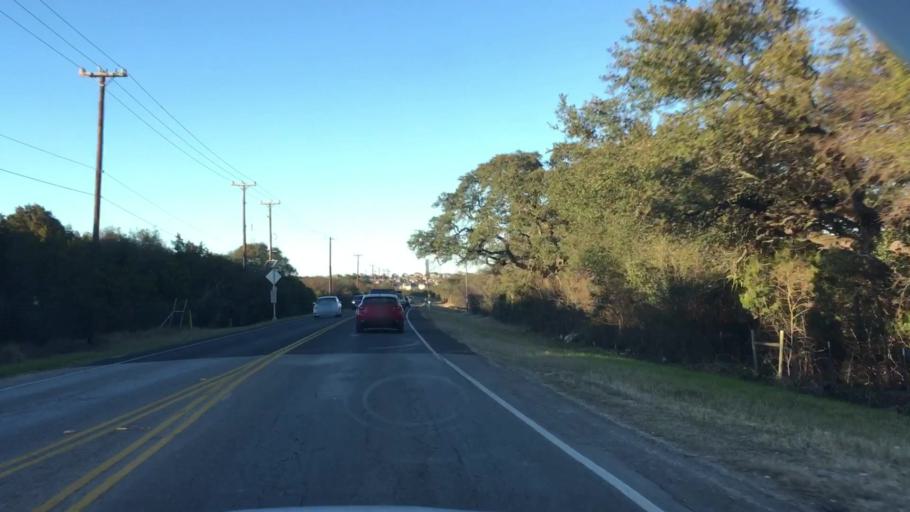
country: US
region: Texas
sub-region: Bexar County
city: Timberwood Park
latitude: 29.6703
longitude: -98.4324
